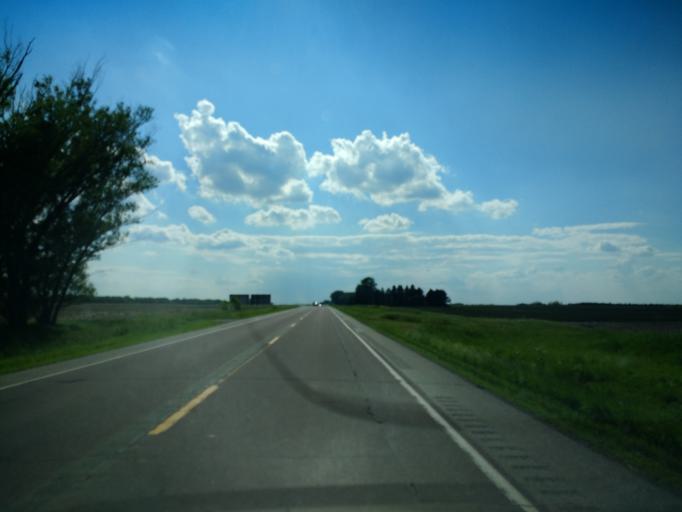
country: US
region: Iowa
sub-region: Clay County
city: Spencer
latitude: 43.1839
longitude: -95.1647
